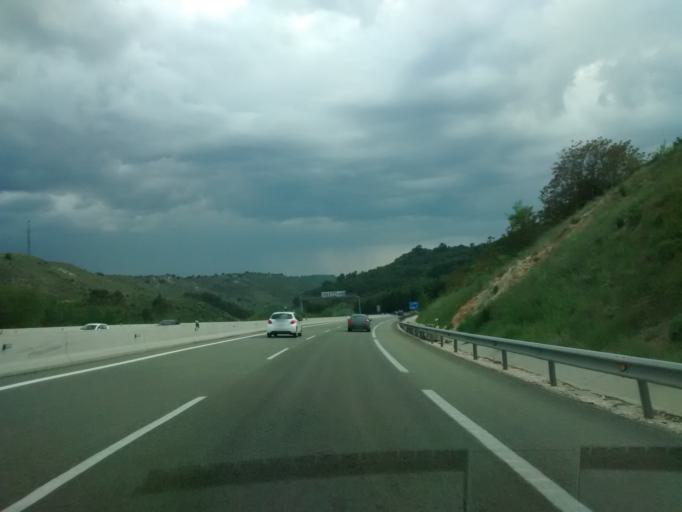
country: ES
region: Castille-La Mancha
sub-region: Provincia de Guadalajara
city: Torija
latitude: 40.7412
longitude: -3.0365
